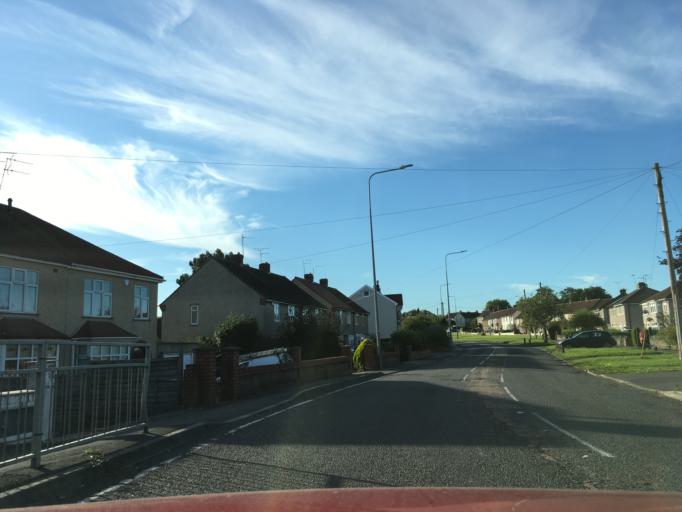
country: GB
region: England
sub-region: South Gloucestershire
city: Mangotsfield
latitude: 51.4878
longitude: -2.4930
